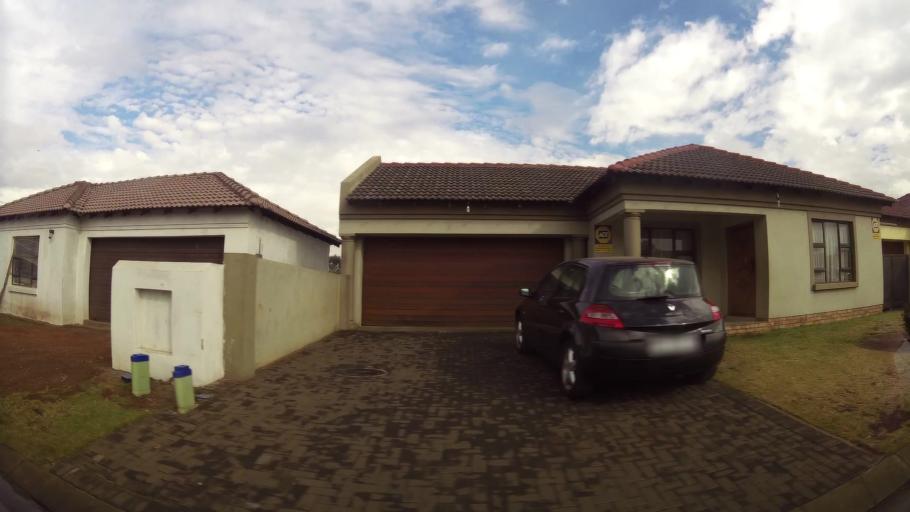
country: ZA
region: Gauteng
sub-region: Ekurhuleni Metropolitan Municipality
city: Germiston
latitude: -26.3290
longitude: 28.1874
